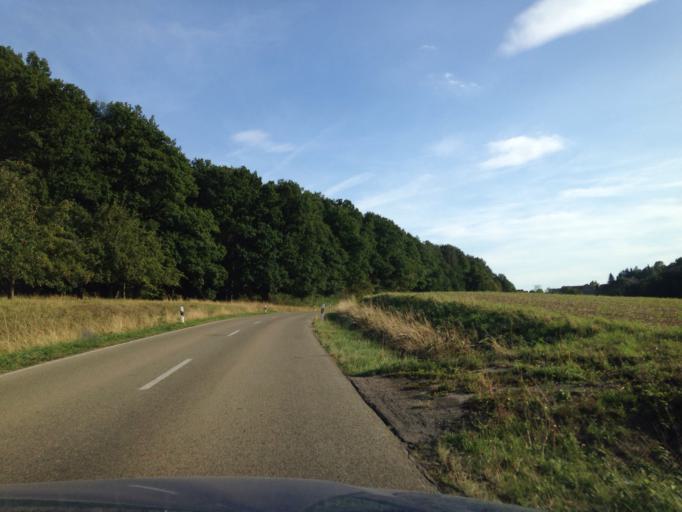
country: DE
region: Bavaria
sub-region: Regierungsbezirk Mittelfranken
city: Thalmassing
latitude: 49.1227
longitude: 11.2130
